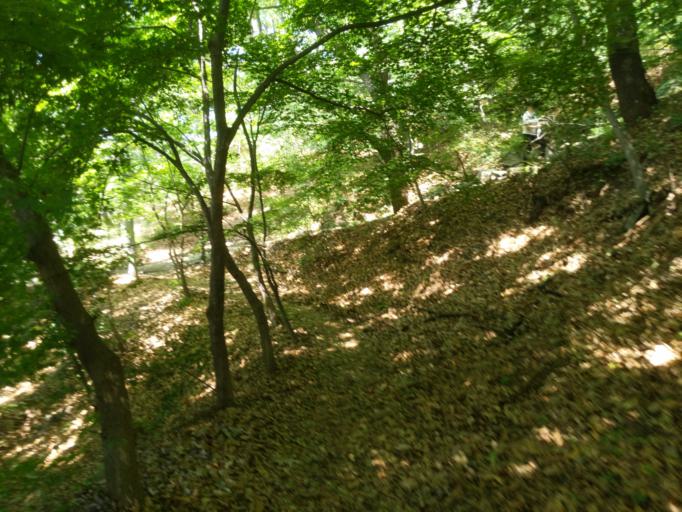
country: KR
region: Seoul
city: Seoul
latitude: 37.6021
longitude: 126.9648
